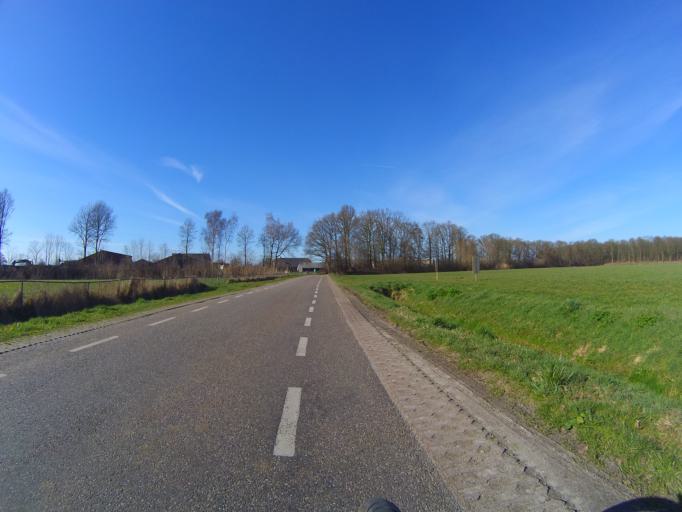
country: NL
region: Utrecht
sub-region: Gemeente Utrechtse Heuvelrug
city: Overberg
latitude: 52.0661
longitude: 5.5151
